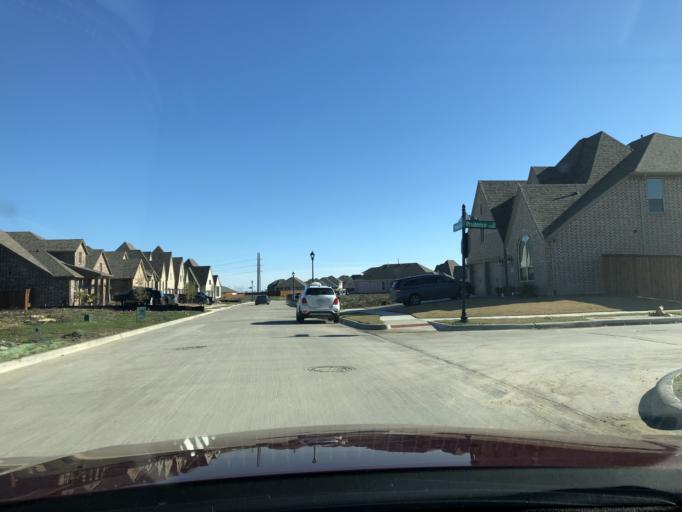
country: US
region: Texas
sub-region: Tarrant County
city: Haslet
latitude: 32.9490
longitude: -97.3963
